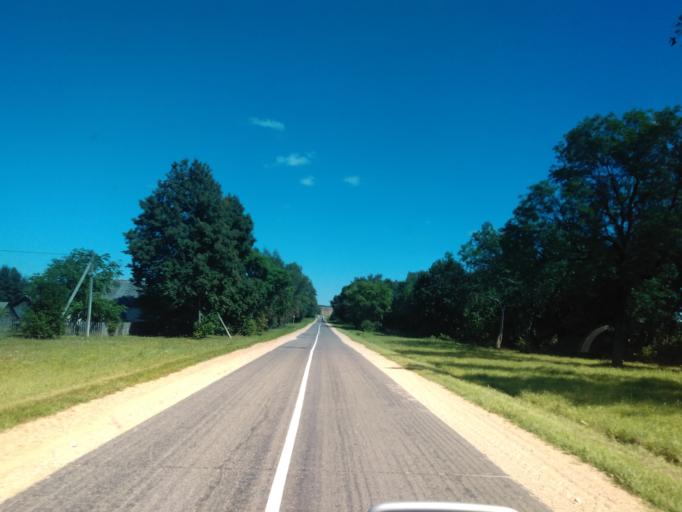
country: BY
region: Minsk
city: Stan'kava
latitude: 53.6345
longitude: 27.2790
